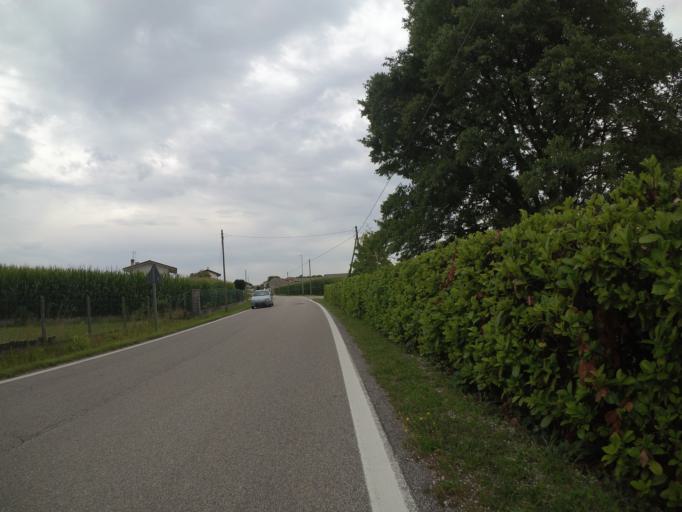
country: IT
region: Friuli Venezia Giulia
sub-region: Provincia di Udine
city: Camino al Tagliamento
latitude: 45.8934
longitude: 12.9544
